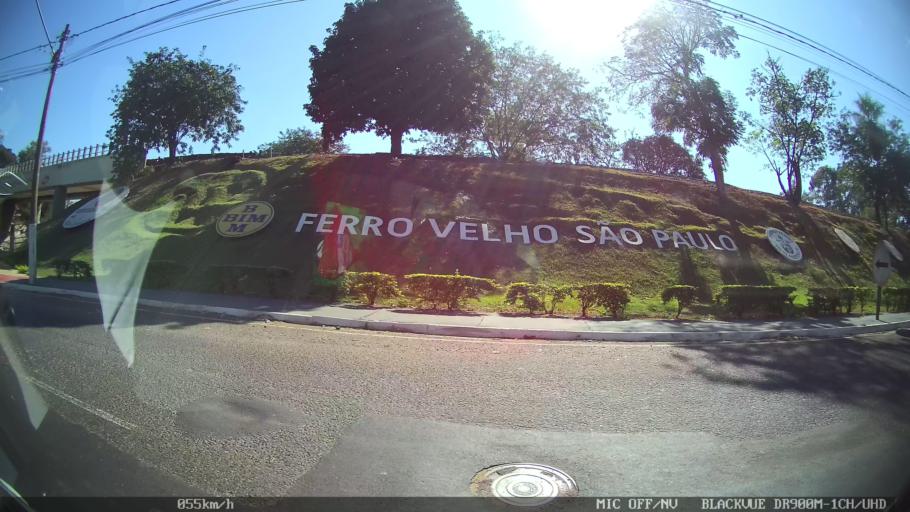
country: BR
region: Sao Paulo
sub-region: Sao Jose Do Rio Preto
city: Sao Jose do Rio Preto
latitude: -20.8150
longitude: -49.4336
